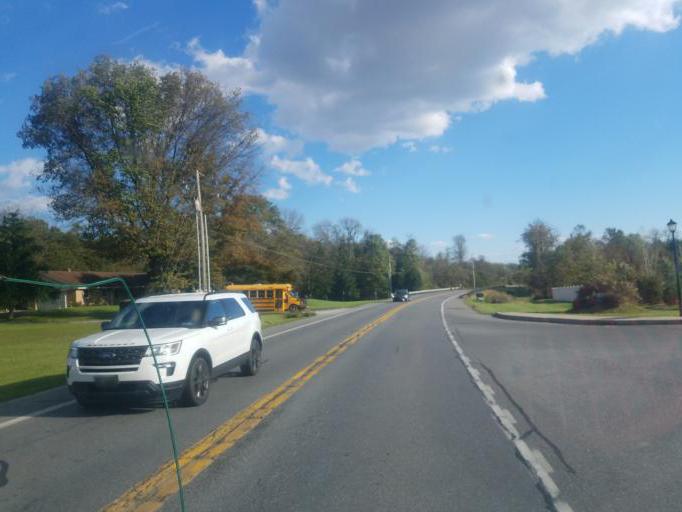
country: US
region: Pennsylvania
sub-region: Lancaster County
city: Bainbridge
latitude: 40.0994
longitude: -76.6689
